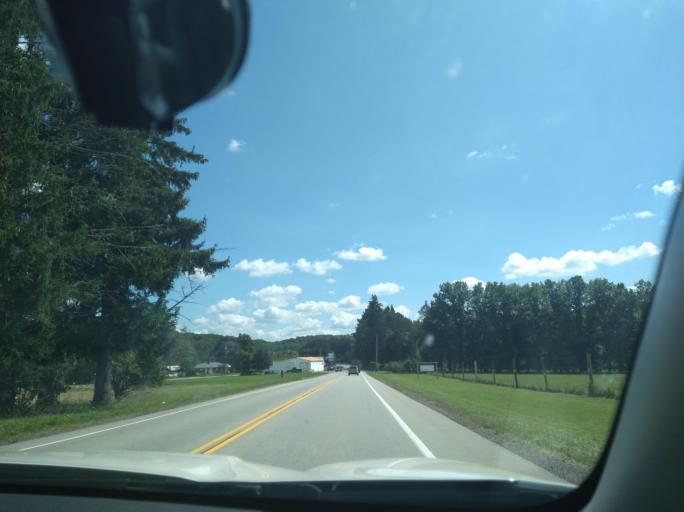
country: US
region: Pennsylvania
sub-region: Somerset County
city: Milford
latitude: 40.0368
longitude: -79.2151
